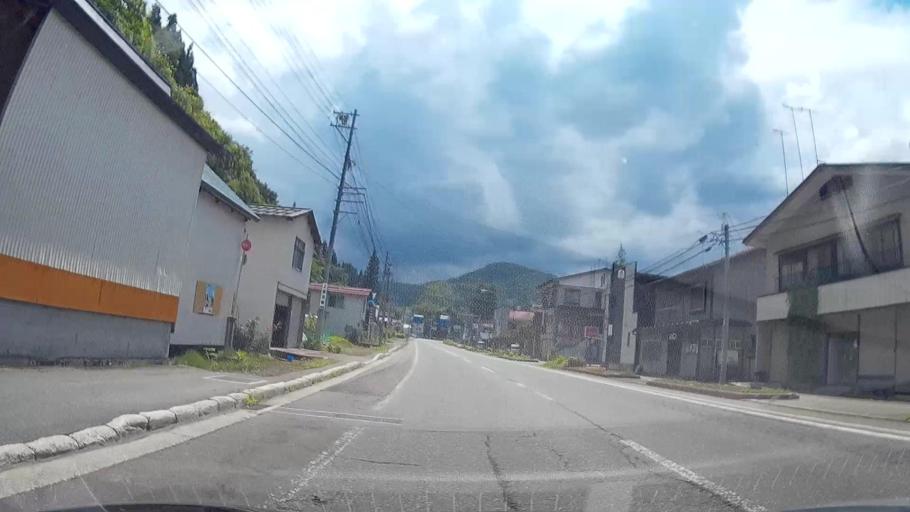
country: JP
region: Niigata
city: Tokamachi
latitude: 36.9920
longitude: 138.5895
